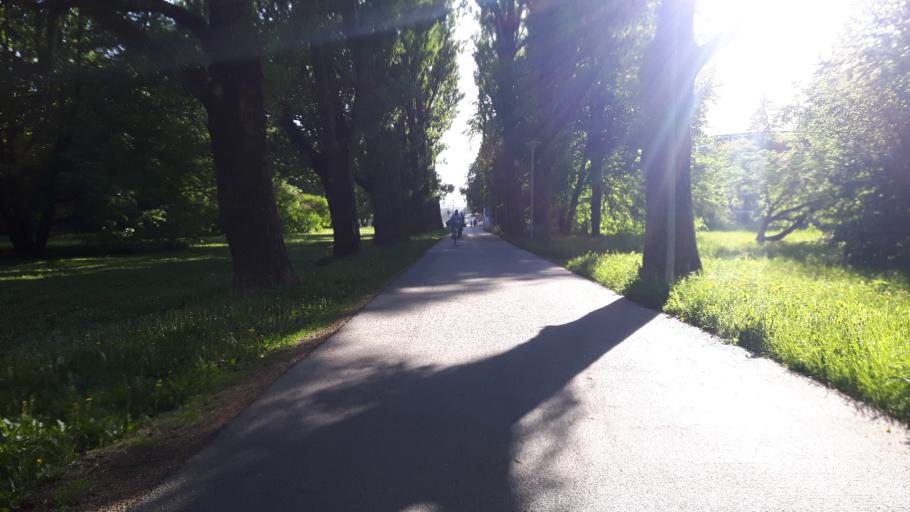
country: EE
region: Harju
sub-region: Tallinna linn
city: Tallinn
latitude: 59.4421
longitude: 24.7874
